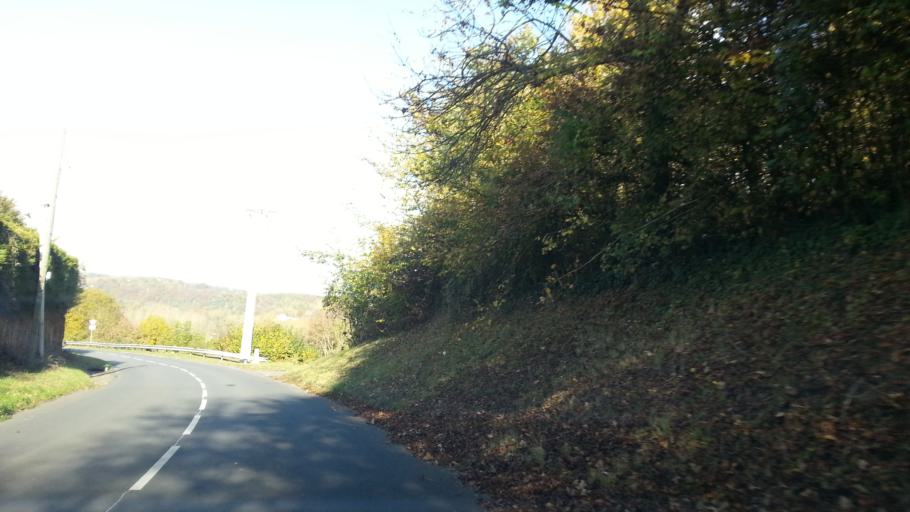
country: FR
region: Picardie
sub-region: Departement de l'Oise
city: Thiverny
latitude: 49.2504
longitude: 2.4046
